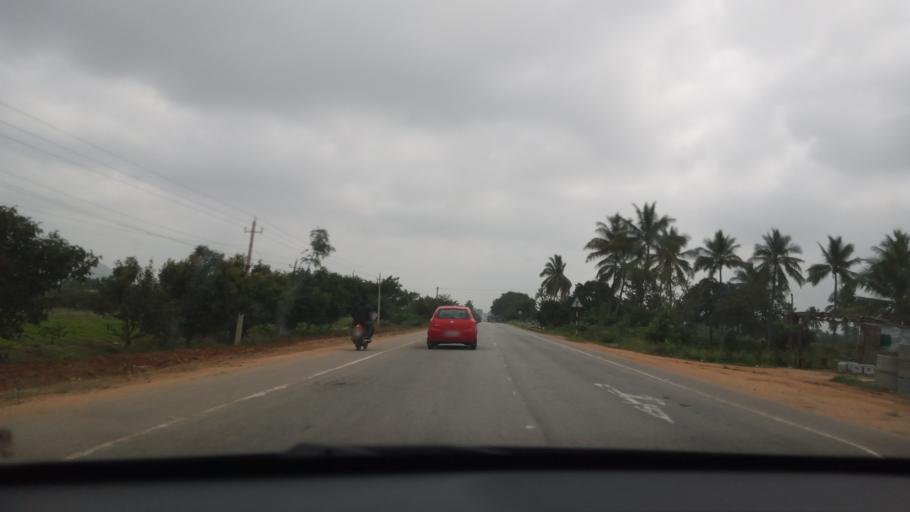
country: IN
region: Karnataka
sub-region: Chikkaballapur
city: Chintamani
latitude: 13.3464
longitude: 78.0188
